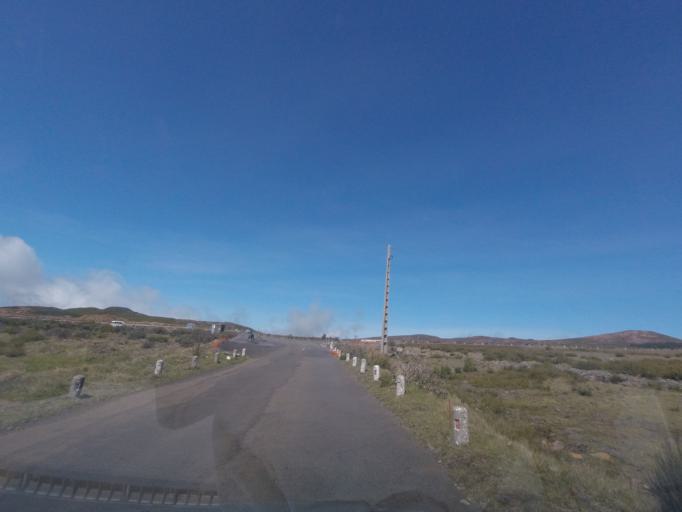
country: PT
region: Madeira
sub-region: Sao Vicente
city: Sao Vicente
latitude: 32.7571
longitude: -17.0970
